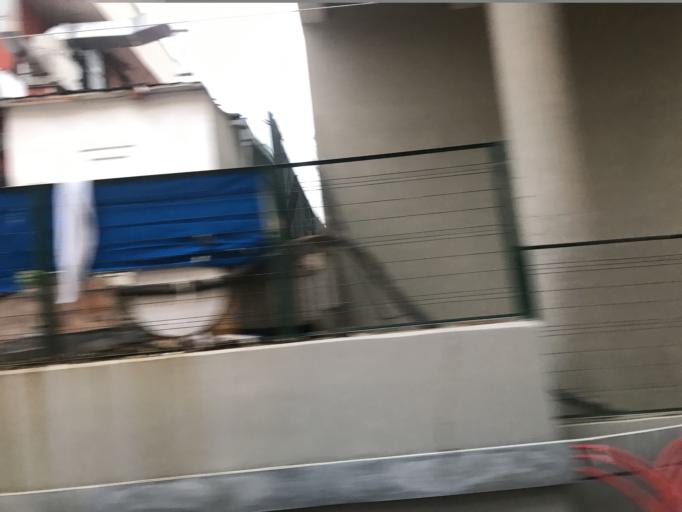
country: TR
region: Istanbul
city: Maltepe
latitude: 40.9378
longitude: 29.1141
